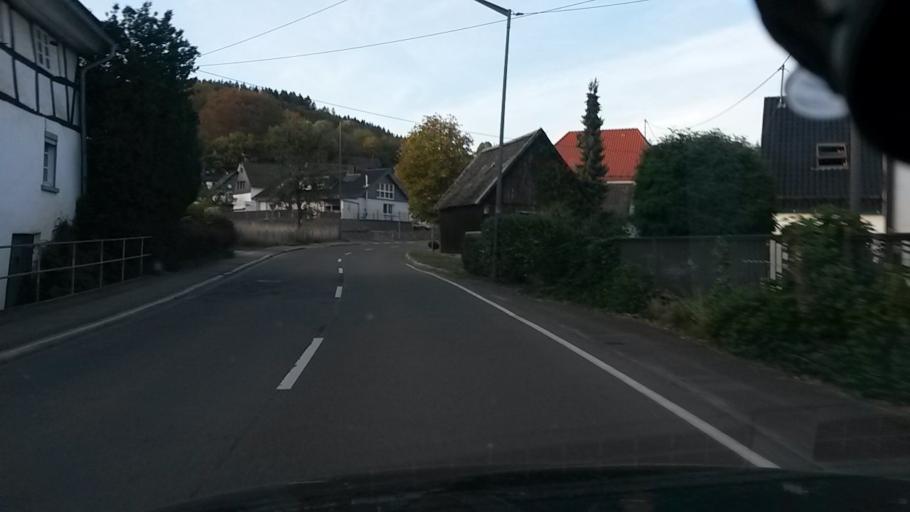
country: DE
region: North Rhine-Westphalia
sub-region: Regierungsbezirk Koln
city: Marienheide
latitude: 51.0749
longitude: 7.5206
